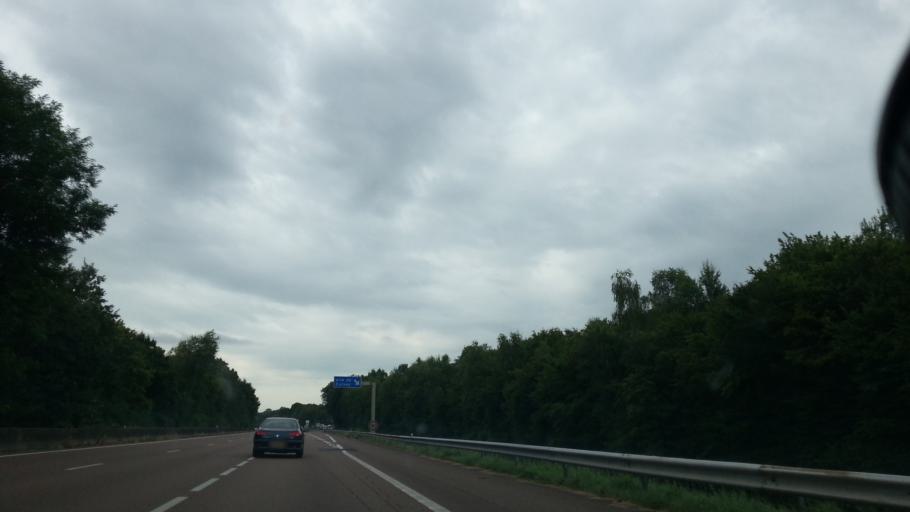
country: FR
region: Bourgogne
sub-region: Departement de Saone-et-Loire
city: Champforgeuil
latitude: 46.8660
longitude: 4.8202
